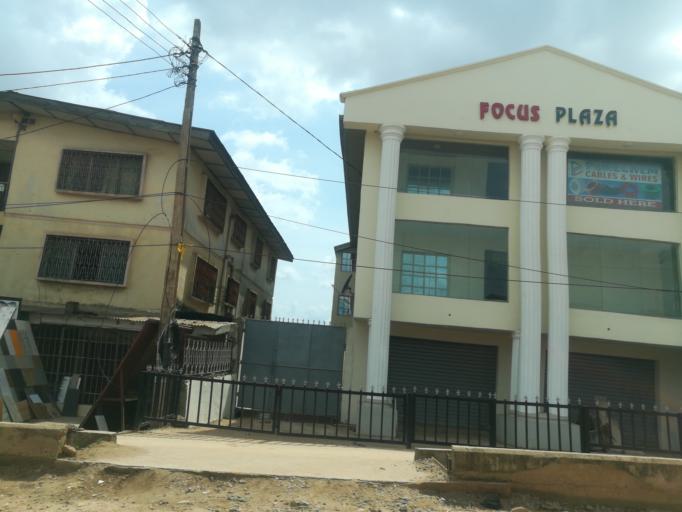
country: NG
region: Oyo
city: Ibadan
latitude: 7.4036
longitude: 3.9329
